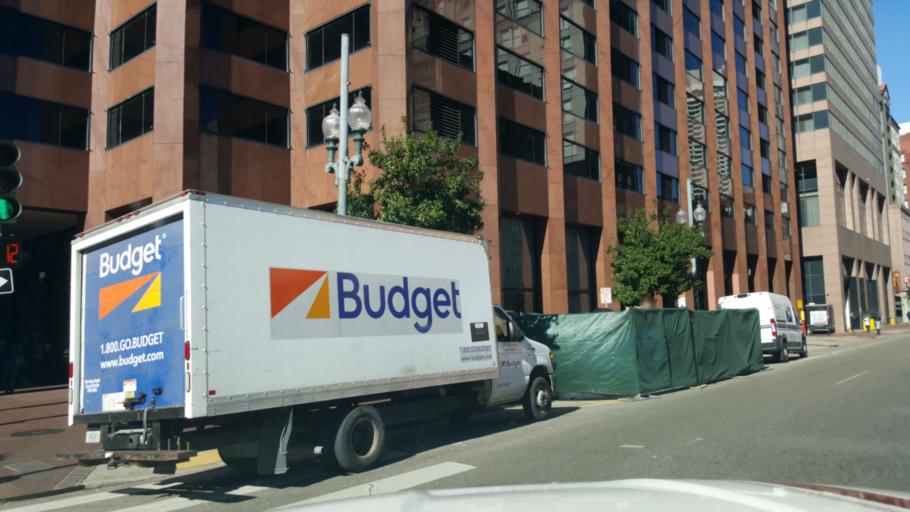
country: US
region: Louisiana
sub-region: Orleans Parish
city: New Orleans
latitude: 29.9494
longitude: -90.0693
